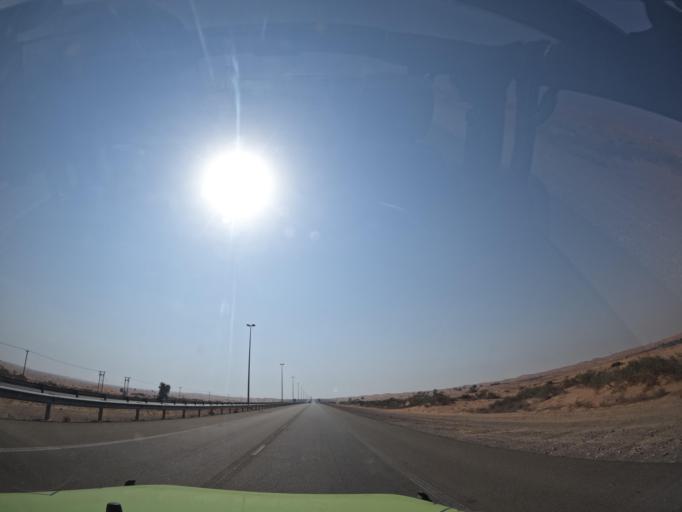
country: OM
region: Al Buraimi
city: Al Buraymi
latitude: 24.4578
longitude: 55.6437
